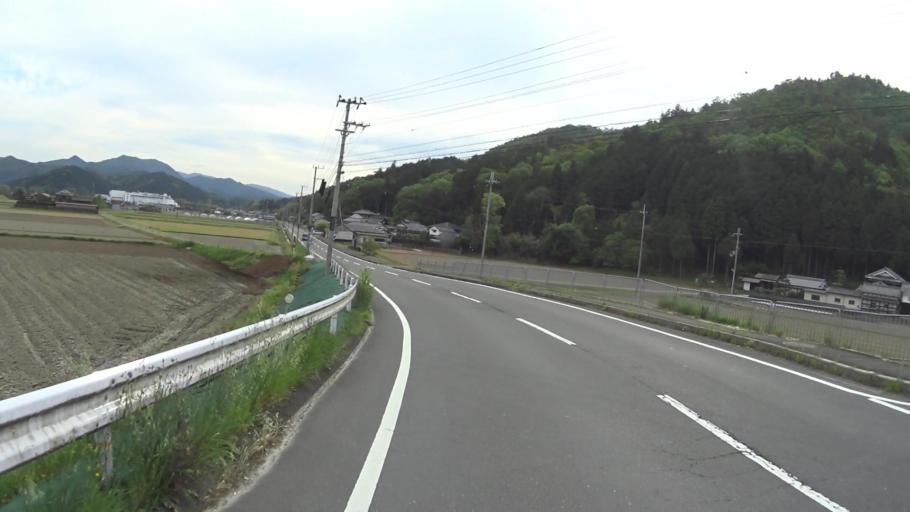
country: JP
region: Kyoto
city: Kameoka
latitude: 35.1029
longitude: 135.5147
